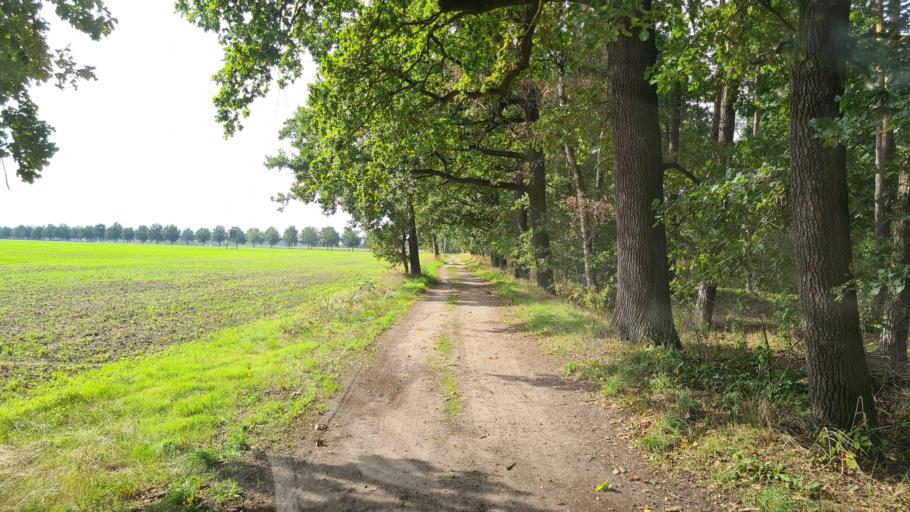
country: DE
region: Brandenburg
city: Schonewalde
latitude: 51.7140
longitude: 13.6048
